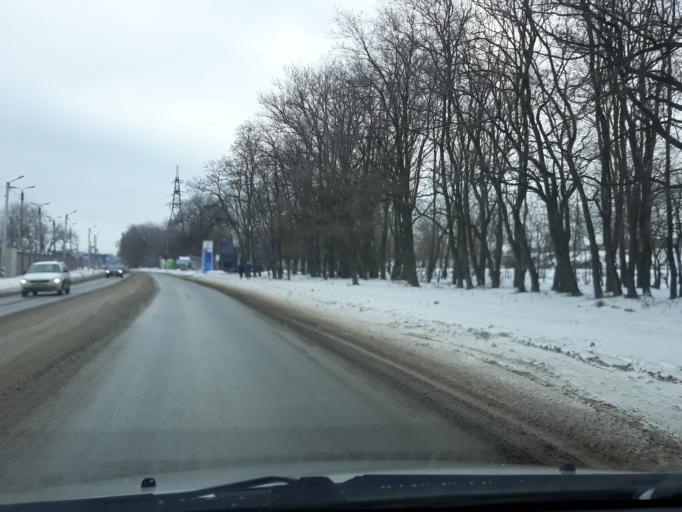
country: RU
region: Rostov
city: Taganrog
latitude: 47.2571
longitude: 38.9042
